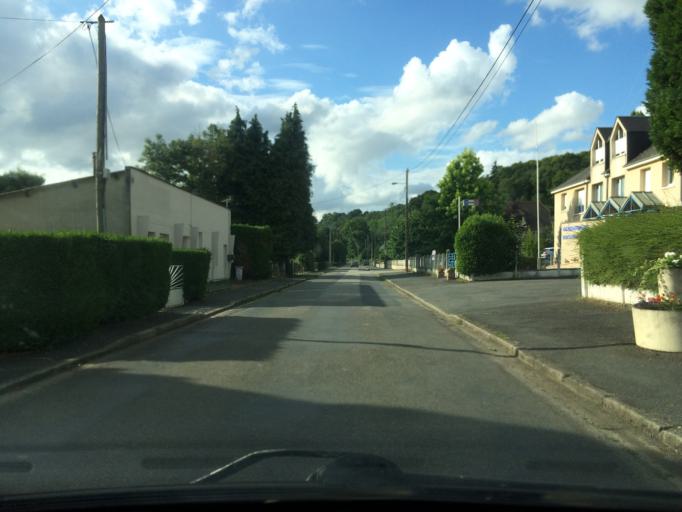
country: FR
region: Lower Normandy
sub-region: Departement du Calvados
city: Clecy
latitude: 48.8753
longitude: -0.4107
